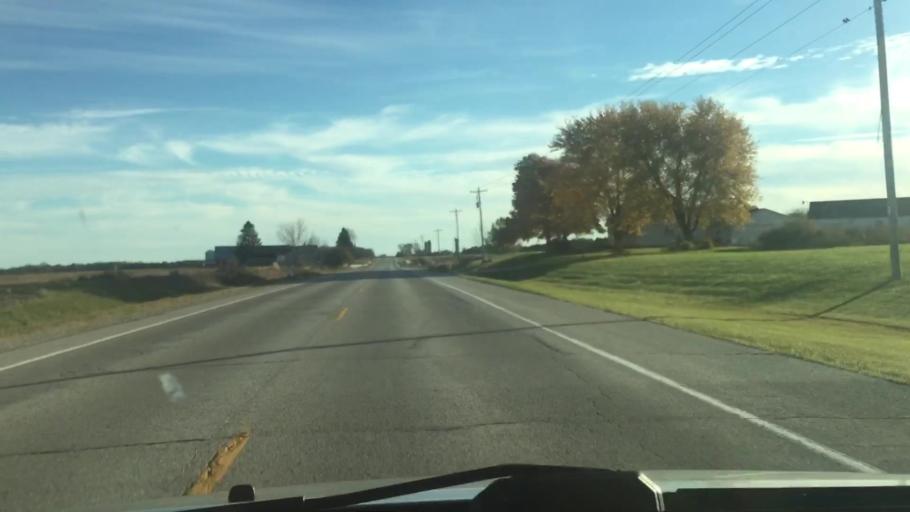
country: US
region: Wisconsin
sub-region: Kewaunee County
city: Kewaunee
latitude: 44.3677
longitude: -87.5424
